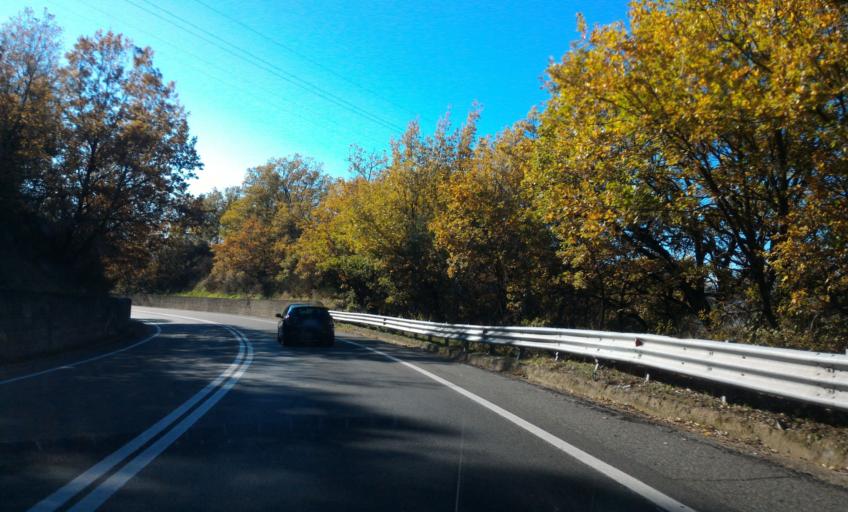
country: IT
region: Calabria
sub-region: Provincia di Cosenza
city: Rovito
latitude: 39.3058
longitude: 16.3096
